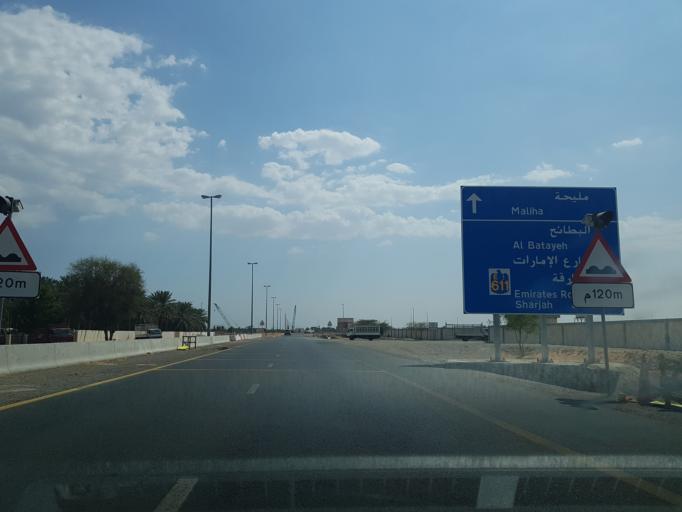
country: AE
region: Ash Shariqah
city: Adh Dhayd
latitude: 25.2353
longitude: 55.9166
